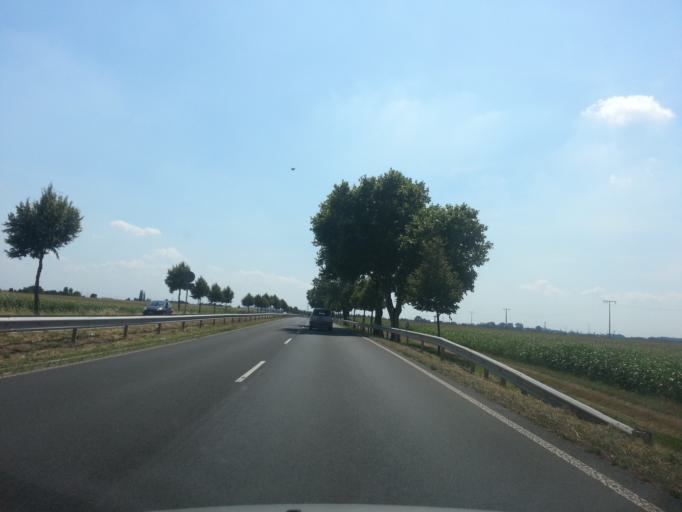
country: DE
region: Hesse
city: Lampertheim
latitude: 49.5766
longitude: 8.4470
